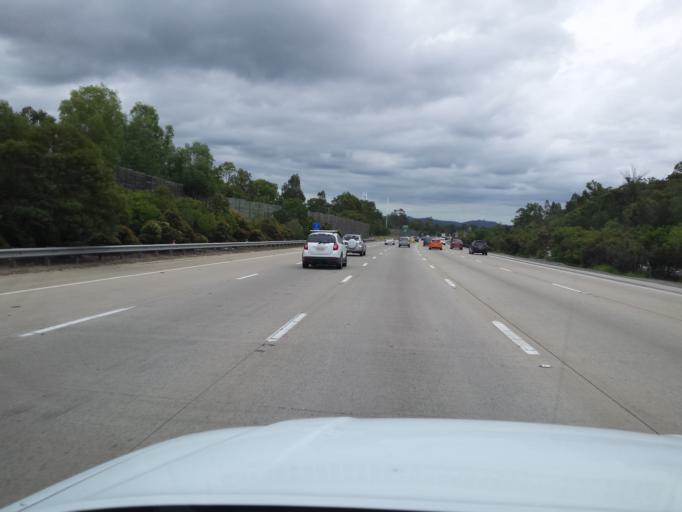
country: AU
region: Queensland
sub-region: Gold Coast
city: Upper Coomera
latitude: -27.9197
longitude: 153.3229
